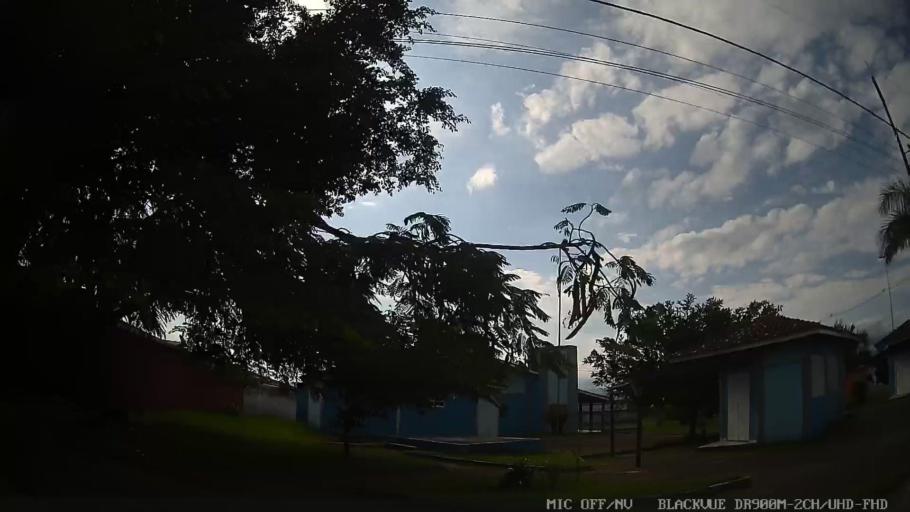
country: BR
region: Sao Paulo
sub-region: Itanhaem
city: Itanhaem
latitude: -24.1795
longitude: -46.8157
